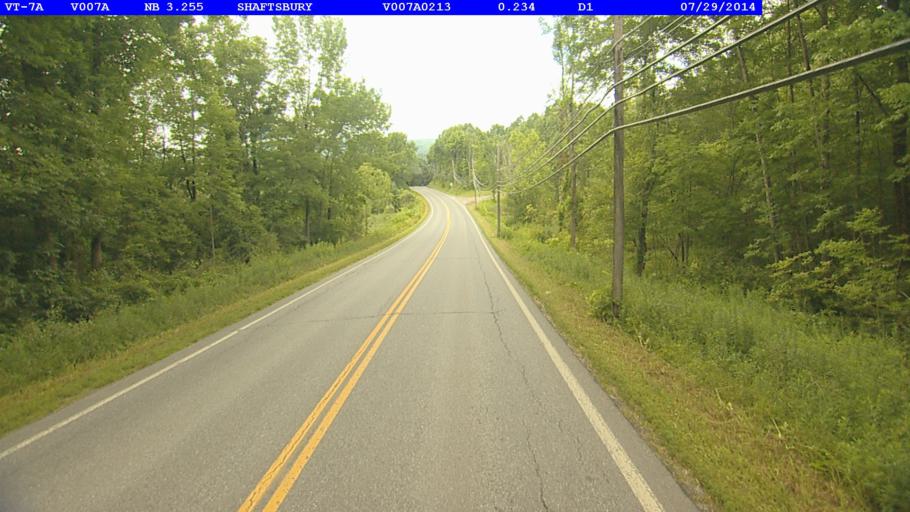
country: US
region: Vermont
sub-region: Bennington County
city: North Bennington
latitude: 42.9361
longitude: -73.2099
